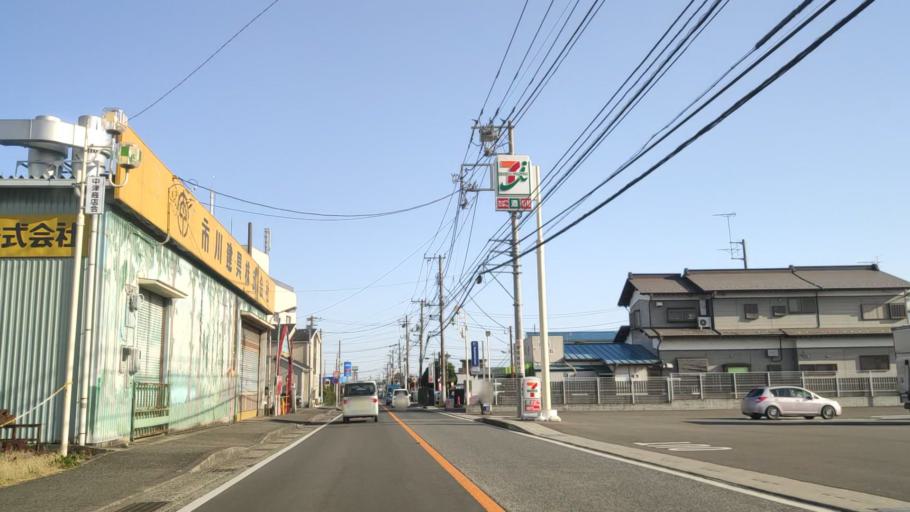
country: JP
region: Kanagawa
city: Zama
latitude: 35.5180
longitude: 139.3325
